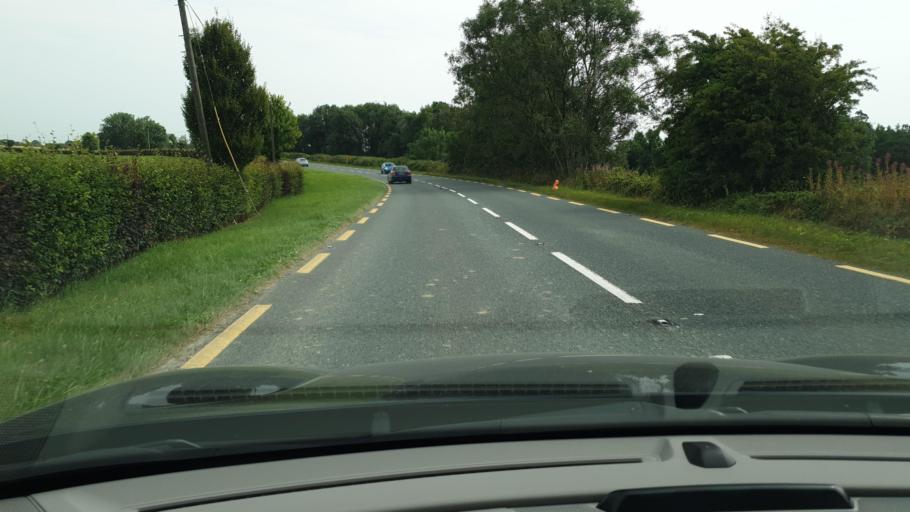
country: IE
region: Leinster
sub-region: An Mhi
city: Kells
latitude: 53.6995
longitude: -6.9244
